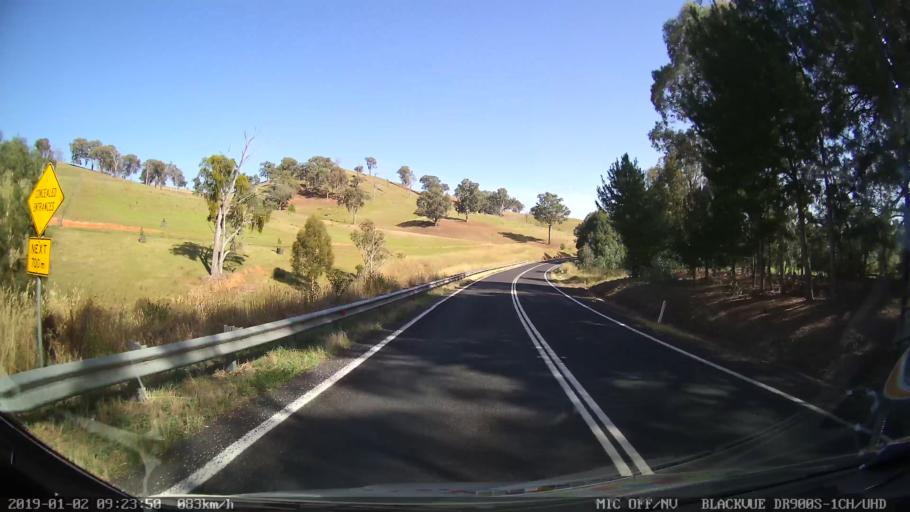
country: AU
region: New South Wales
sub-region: Tumut Shire
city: Tumut
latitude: -35.3846
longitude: 148.2920
